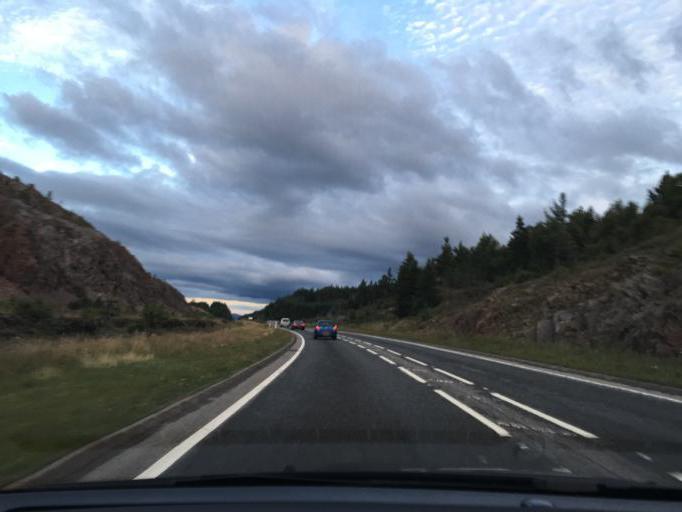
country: GB
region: Scotland
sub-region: Highland
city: Aviemore
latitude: 57.2913
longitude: -3.9110
